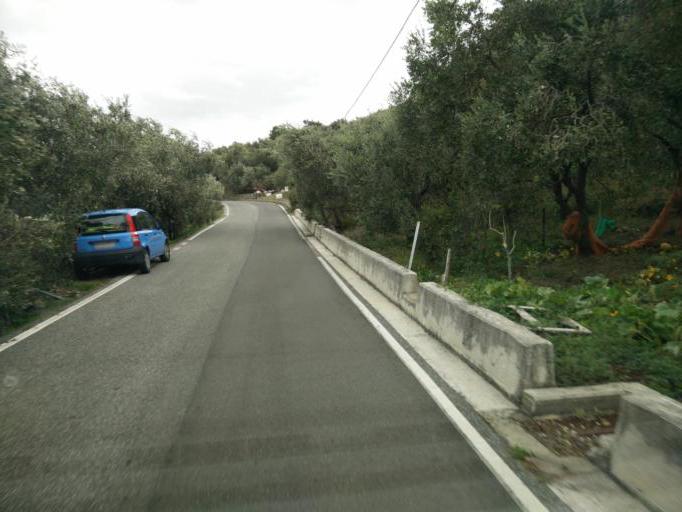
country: IT
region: Liguria
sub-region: Provincia di La Spezia
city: Riomaggiore
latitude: 44.1163
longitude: 9.7285
